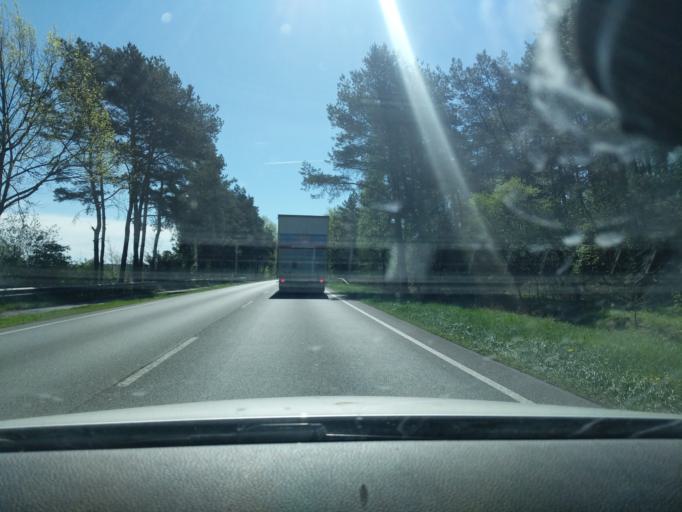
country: DE
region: Lower Saxony
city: Buxtehude
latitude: 53.4575
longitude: 9.7234
